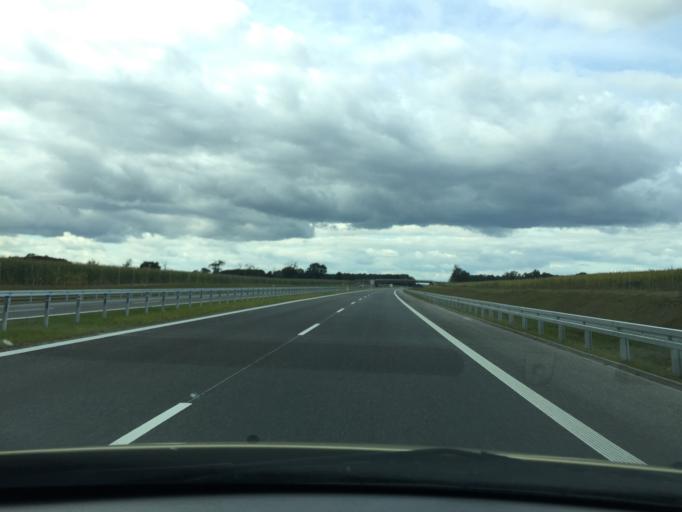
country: PL
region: Greater Poland Voivodeship
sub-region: Powiat jarocinski
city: Jarocin
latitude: 51.9861
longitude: 17.5123
